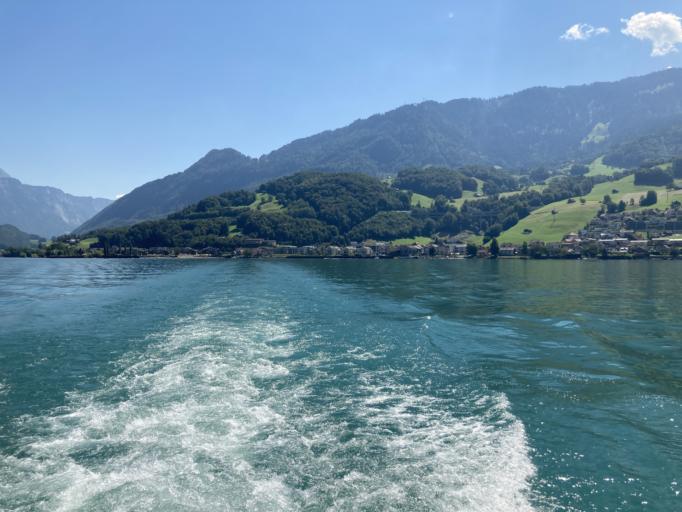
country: CH
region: Saint Gallen
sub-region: Wahlkreis Sarganserland
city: Quarten
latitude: 47.1184
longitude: 9.2443
